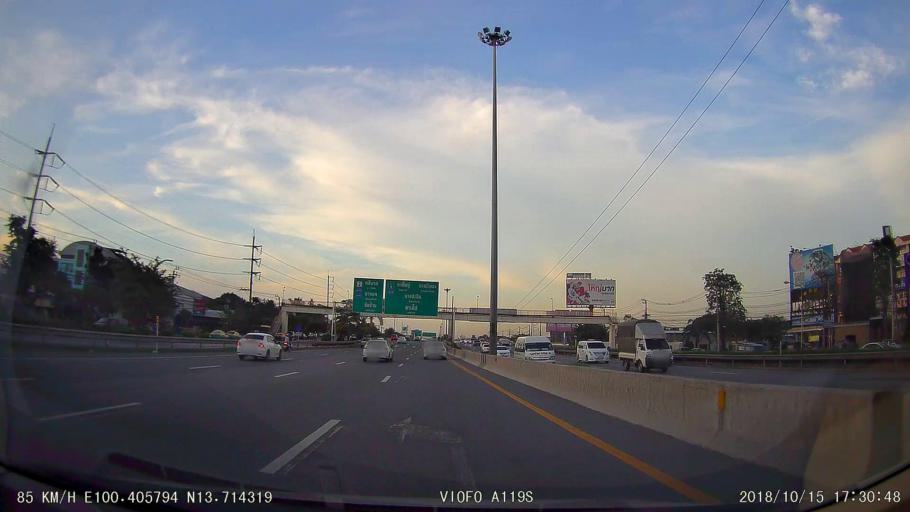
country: TH
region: Bangkok
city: Bang Khae
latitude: 13.7145
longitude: 100.4058
